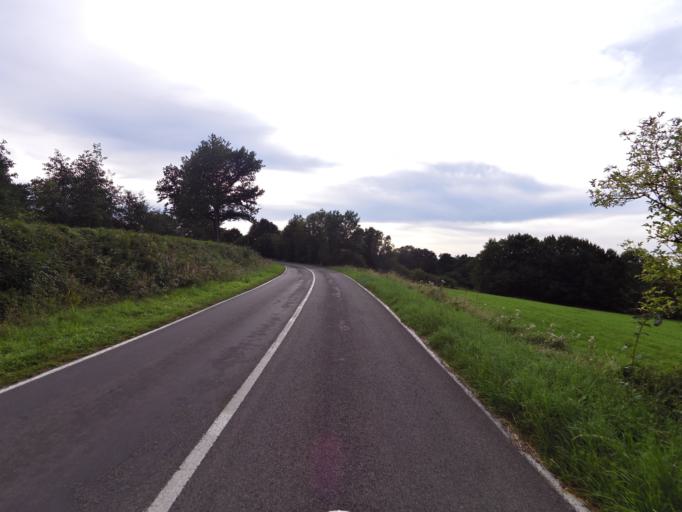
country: BE
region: Wallonia
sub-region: Province du Luxembourg
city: Erezee
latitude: 50.2957
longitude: 5.5432
